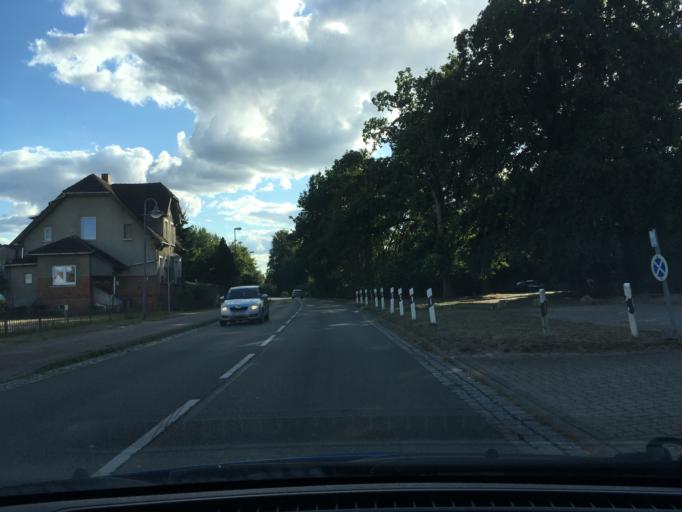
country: DE
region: Mecklenburg-Vorpommern
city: Neustadt-Glewe
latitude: 53.3813
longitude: 11.5767
